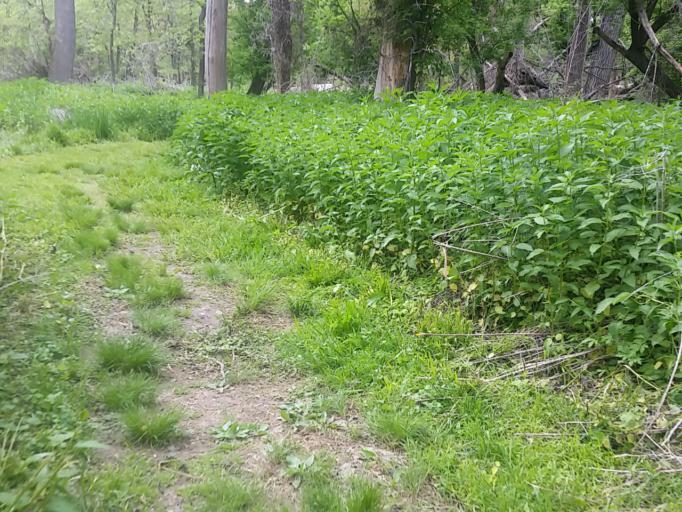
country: US
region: Nebraska
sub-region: Sarpy County
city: Bellevue
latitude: 41.1822
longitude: -95.9022
